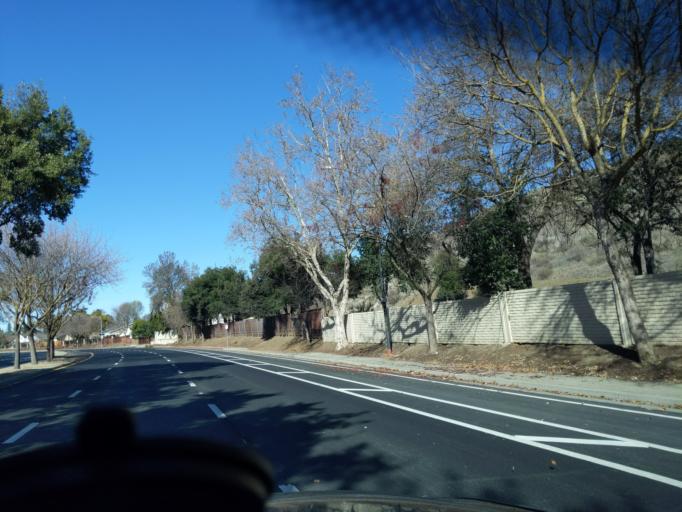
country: US
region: California
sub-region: Santa Clara County
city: Seven Trees
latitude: 37.2209
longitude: -121.7626
